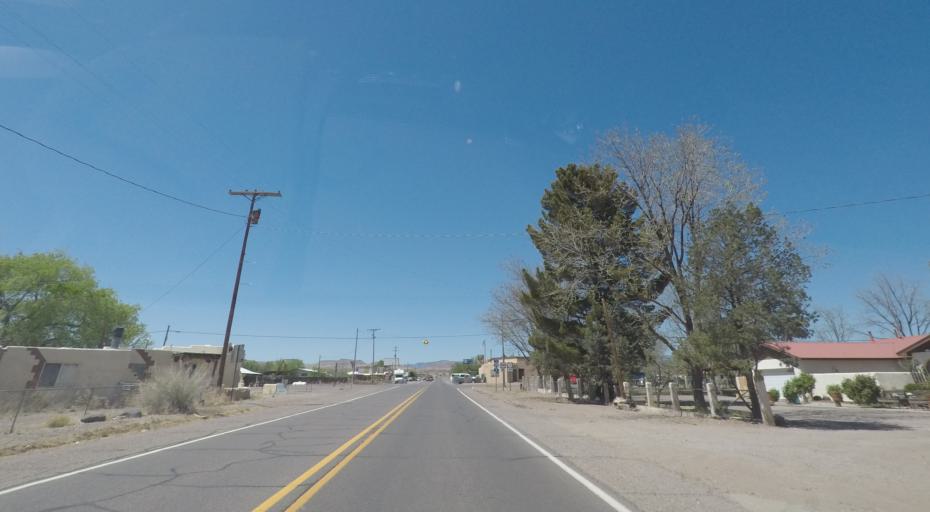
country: US
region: New Mexico
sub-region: Socorro County
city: Socorro
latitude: 33.9179
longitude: -106.8666
